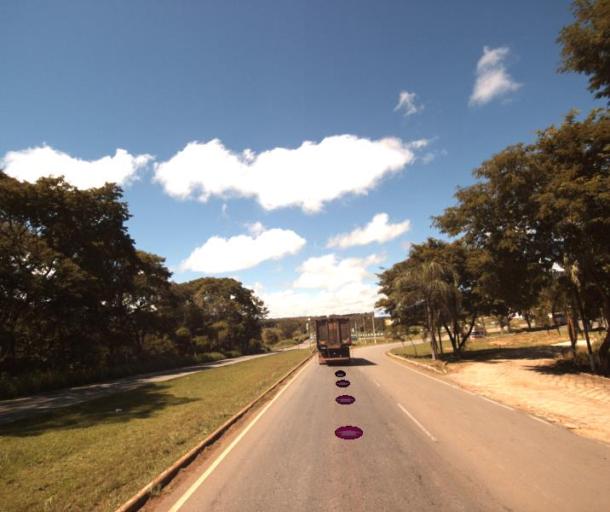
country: BR
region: Goias
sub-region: Jaragua
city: Jaragua
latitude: -15.7578
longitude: -49.3137
